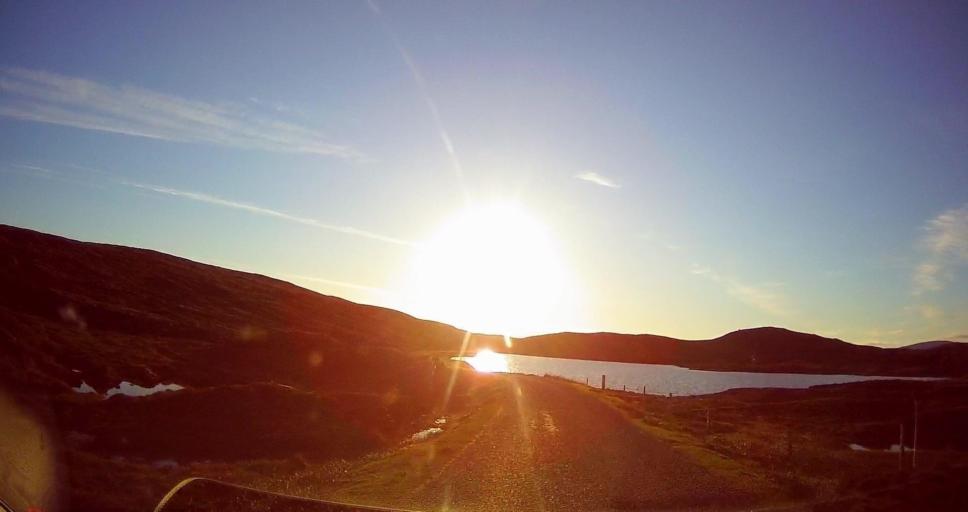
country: GB
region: Scotland
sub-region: Shetland Islands
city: Lerwick
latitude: 60.4423
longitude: -1.4036
